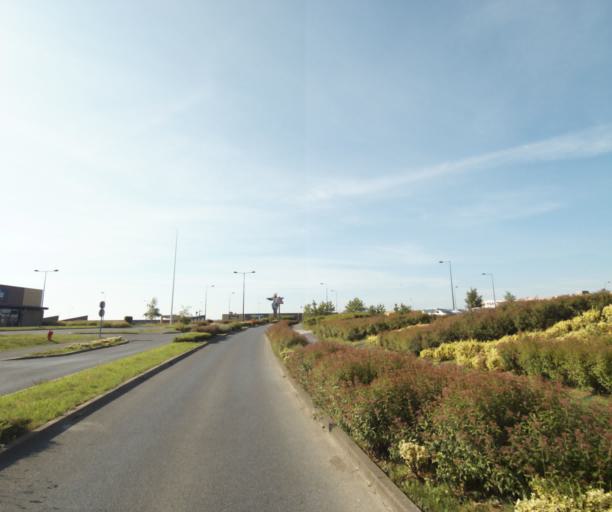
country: FR
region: Champagne-Ardenne
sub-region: Departement des Ardennes
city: La Francheville
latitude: 49.7372
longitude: 4.7078
